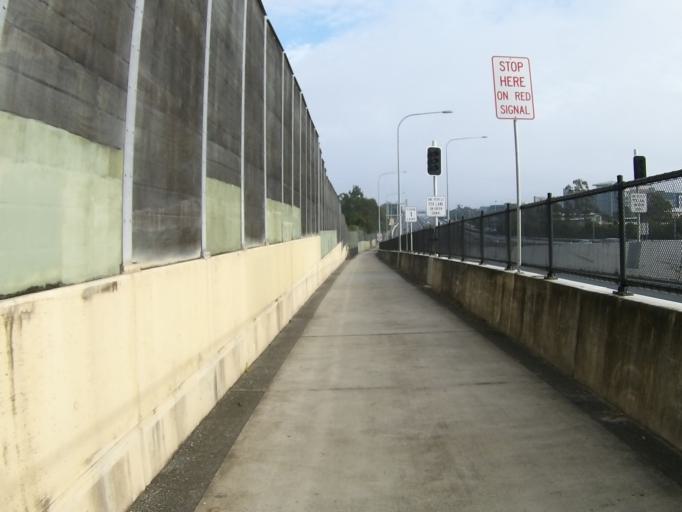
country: AU
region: Queensland
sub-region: Brisbane
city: Upper Mount Gravatt
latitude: -27.5695
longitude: 153.0887
